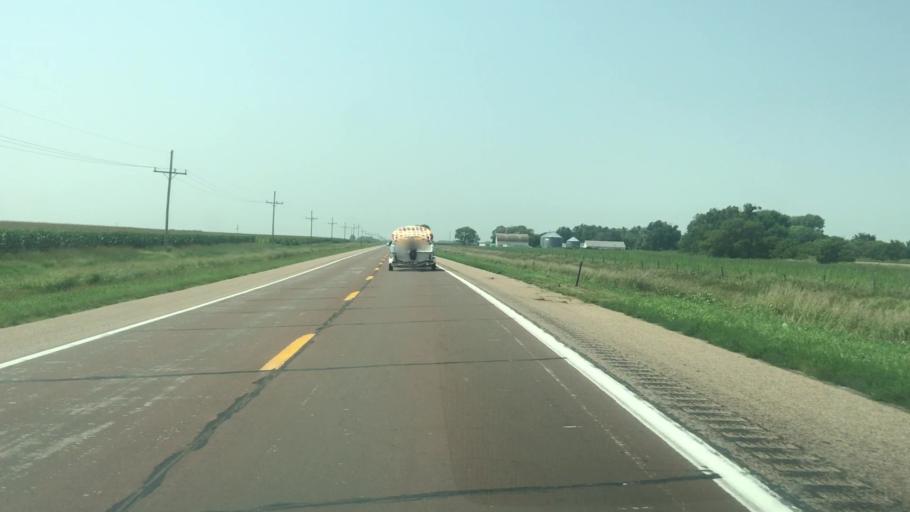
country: US
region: Nebraska
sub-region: Hall County
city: Grand Island
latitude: 40.9673
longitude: -98.4480
